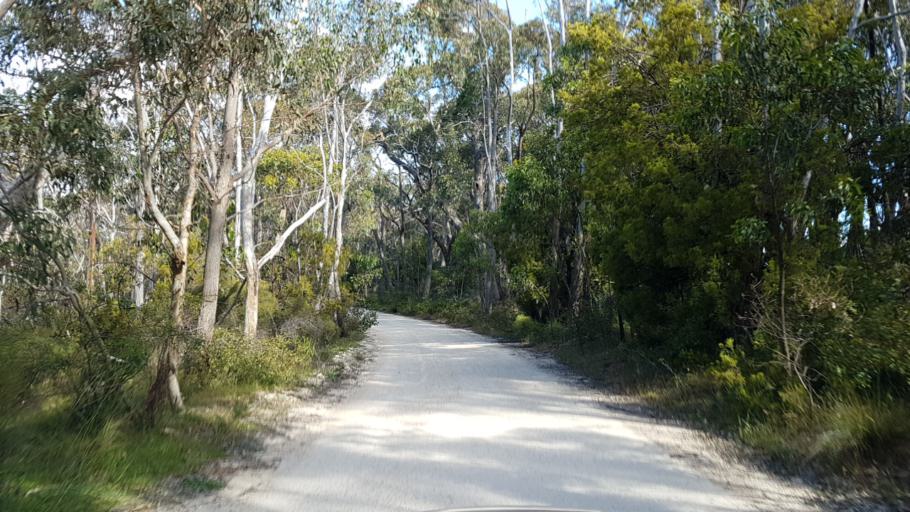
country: AU
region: South Australia
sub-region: Adelaide Hills
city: Adelaide Hills
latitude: -34.9030
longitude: 138.7296
